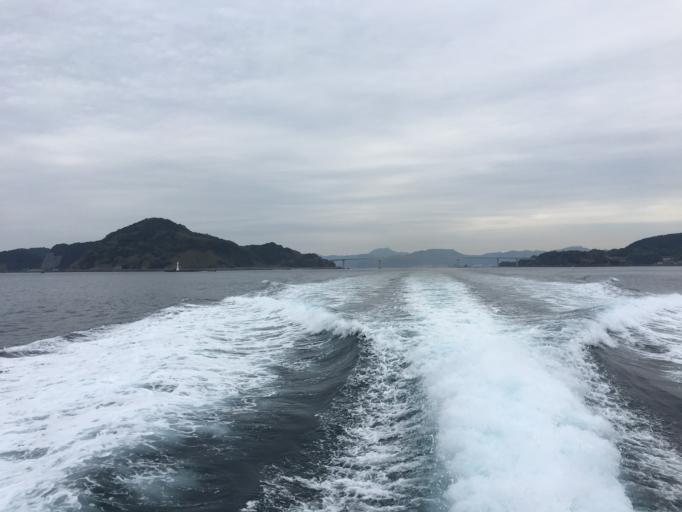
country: JP
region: Nagasaki
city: Nagasaki-shi
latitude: 32.6771
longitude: 129.7803
